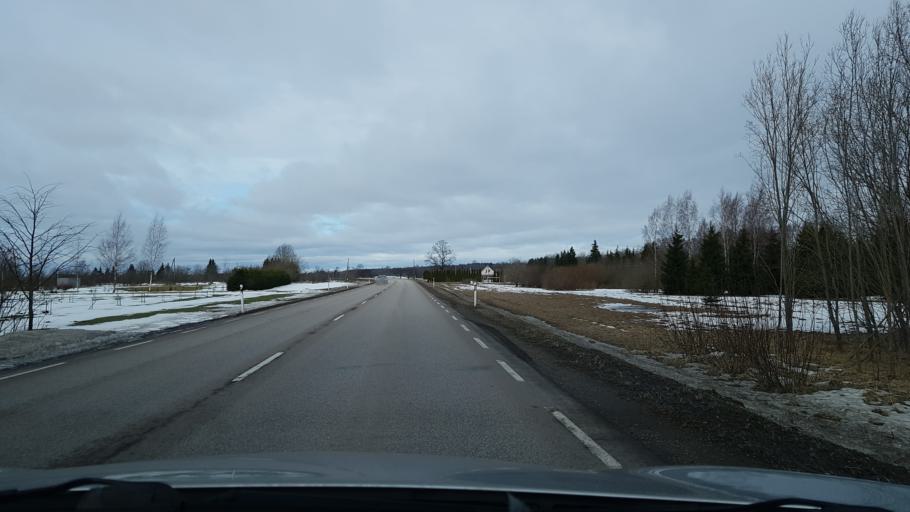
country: EE
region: Jogevamaa
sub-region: Jogeva linn
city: Jogeva
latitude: 58.6765
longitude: 26.4879
